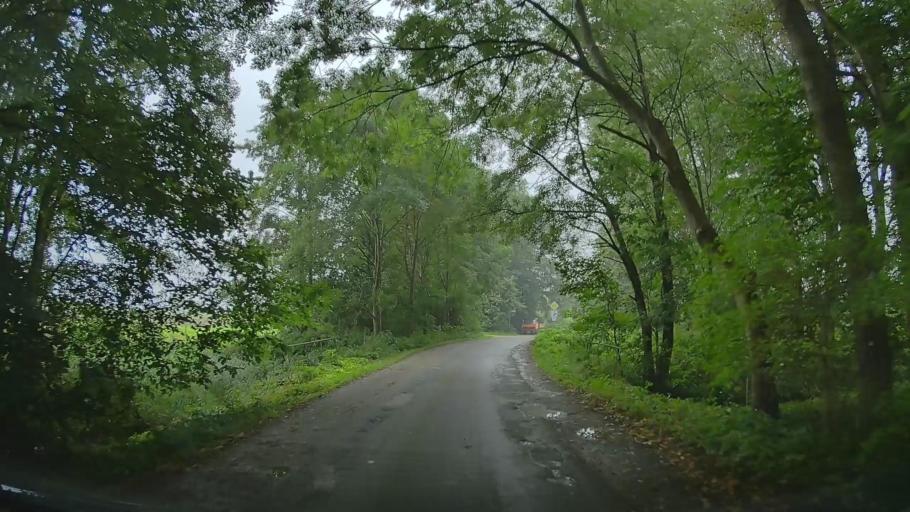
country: DE
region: Mecklenburg-Vorpommern
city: Gramkow
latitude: 53.9280
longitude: 11.3609
